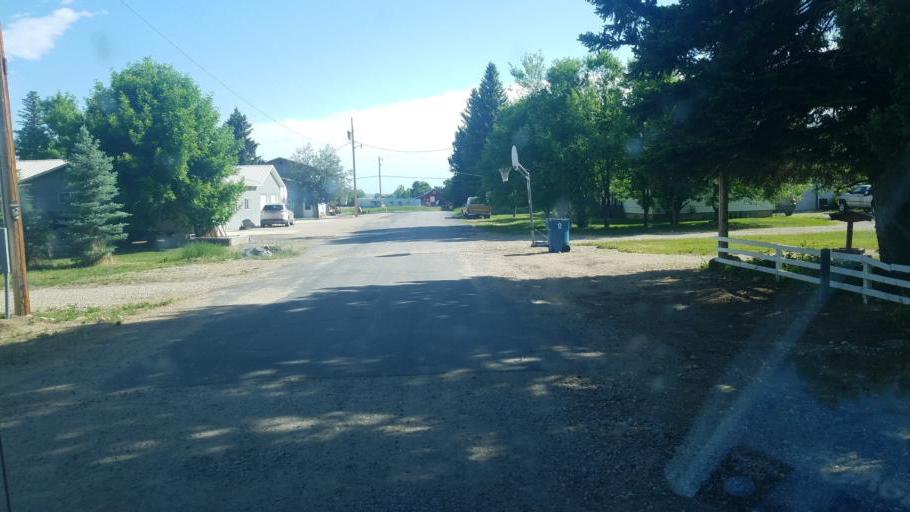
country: US
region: Montana
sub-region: Carbon County
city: Red Lodge
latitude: 45.3590
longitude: -109.1643
